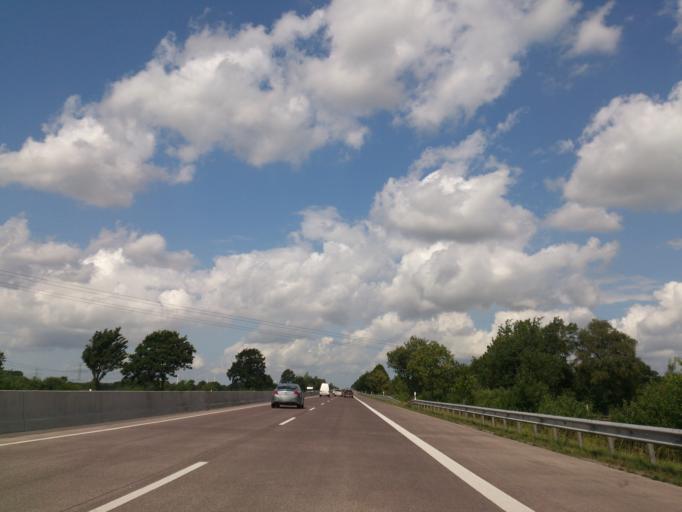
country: DE
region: Schleswig-Holstein
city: Klein Offenseth-Sparrieshoop
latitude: 53.8136
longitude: 9.6632
